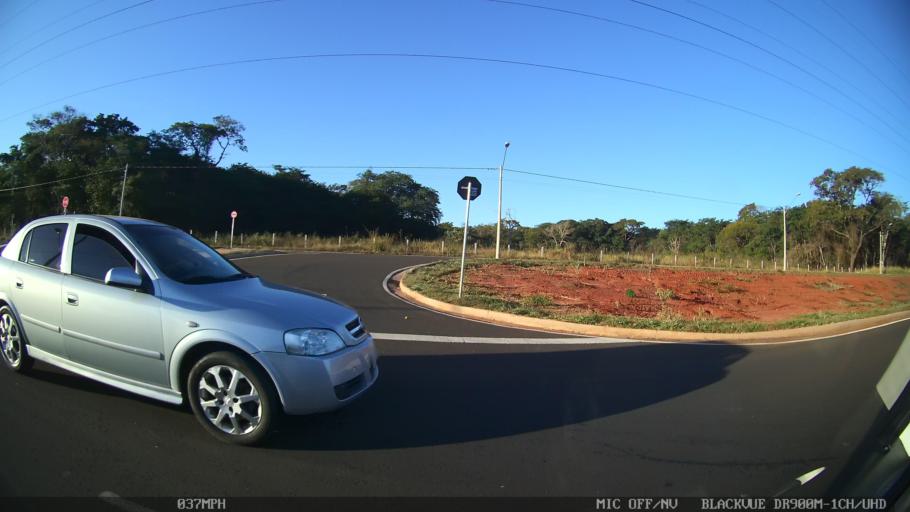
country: BR
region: Sao Paulo
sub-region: Sao Jose Do Rio Preto
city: Sao Jose do Rio Preto
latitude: -20.7702
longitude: -49.3531
